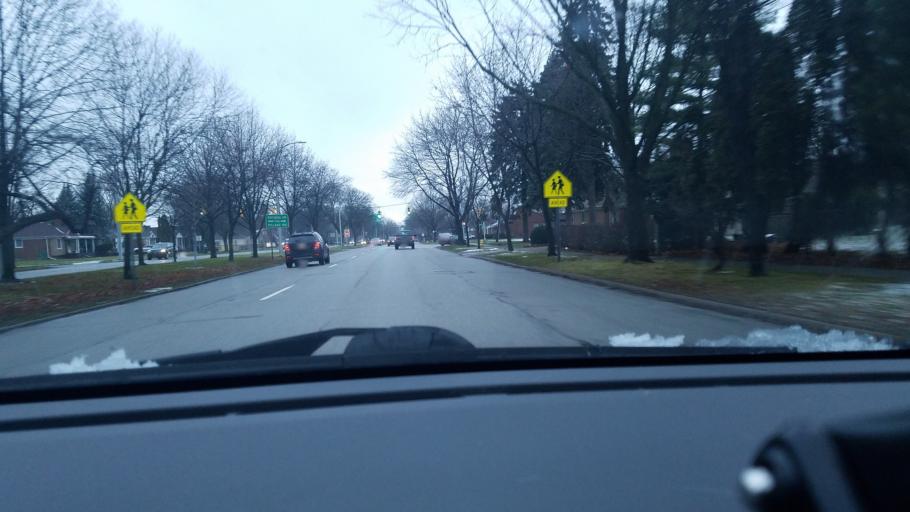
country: US
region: Michigan
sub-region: Wayne County
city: Allen Park
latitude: 42.2888
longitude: -83.2420
